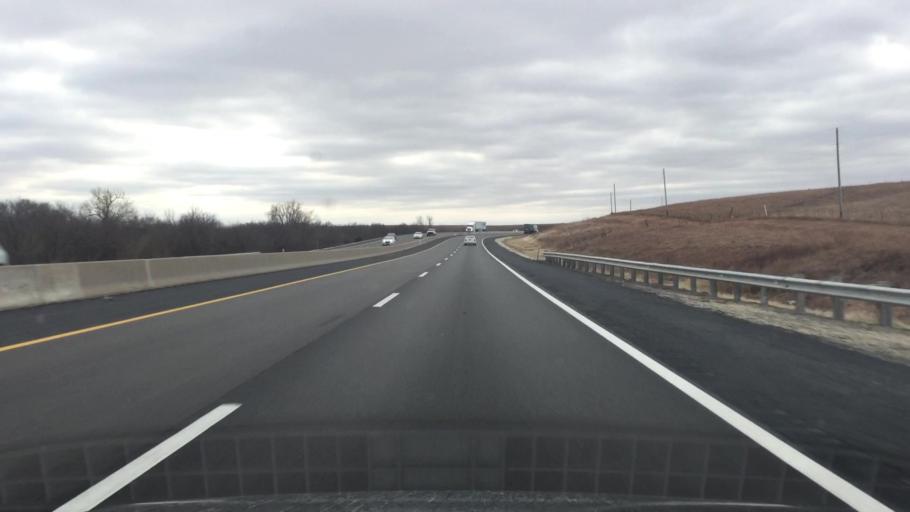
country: US
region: Kansas
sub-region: Chase County
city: Cottonwood Falls
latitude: 38.1528
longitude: -96.4923
